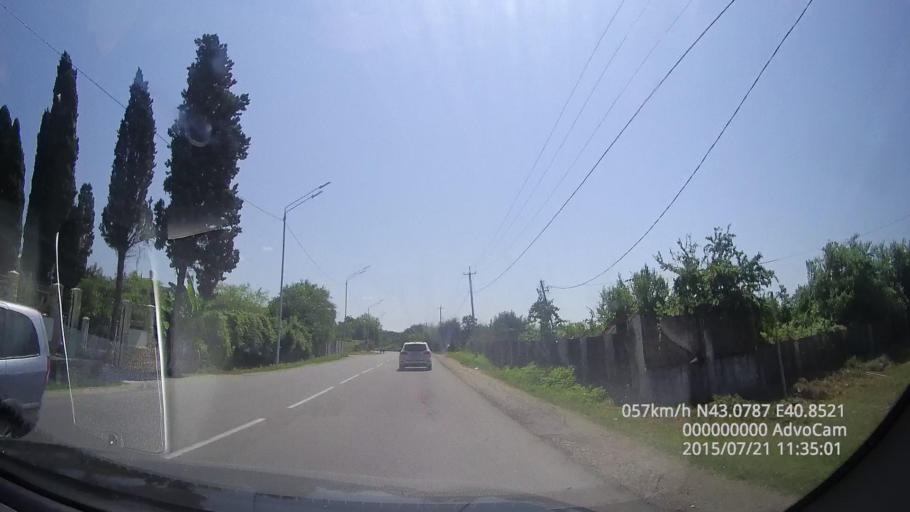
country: GE
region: Abkhazia
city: Stantsiya Novyy Afon
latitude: 43.0785
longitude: 40.8527
